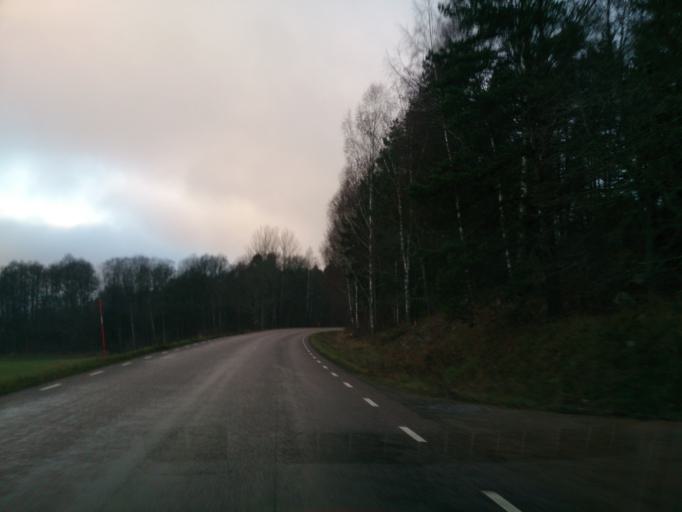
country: SE
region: OEstergoetland
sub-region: Atvidabergs Kommun
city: Atvidaberg
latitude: 58.2903
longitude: 16.0064
